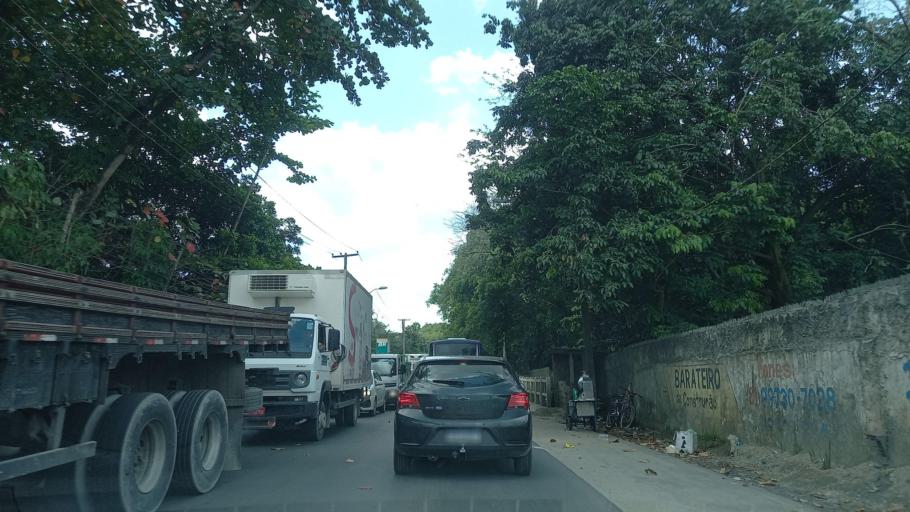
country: BR
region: Pernambuco
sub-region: Jaboatao Dos Guararapes
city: Jaboatao dos Guararapes
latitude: -8.1113
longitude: -35.0072
